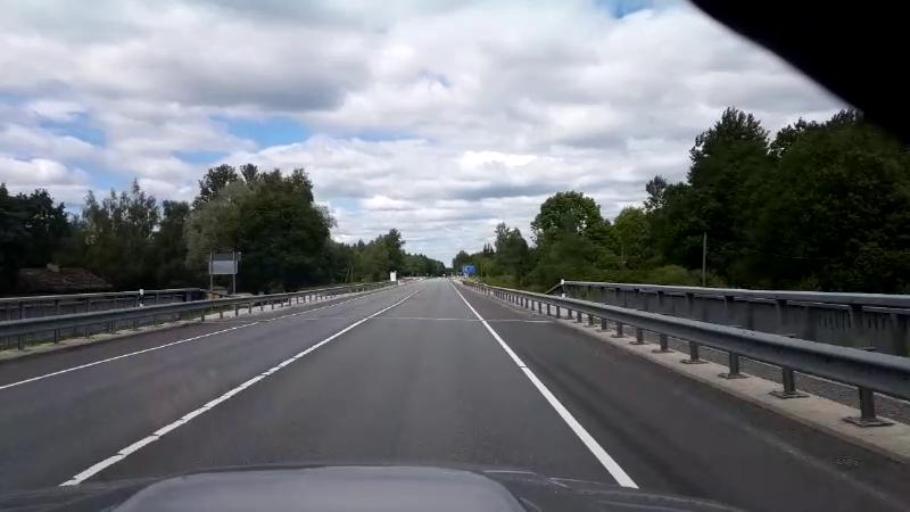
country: EE
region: Raplamaa
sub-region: Maerjamaa vald
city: Marjamaa
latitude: 58.8106
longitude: 24.4126
